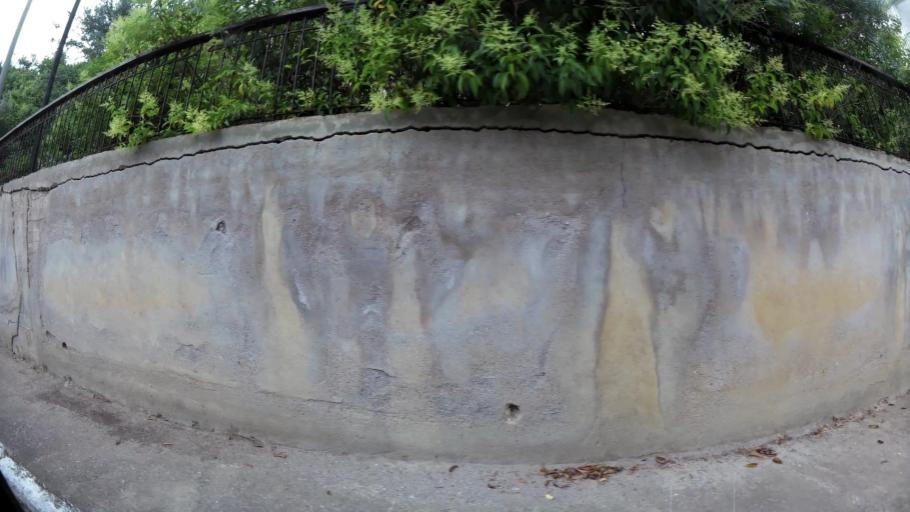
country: GR
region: Central Macedonia
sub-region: Nomos Thessalonikis
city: Oraiokastro
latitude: 40.7087
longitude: 22.9286
